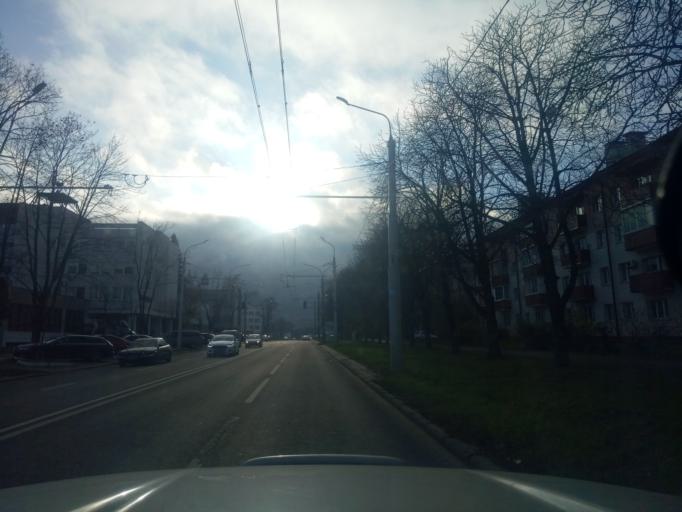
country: BY
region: Minsk
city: Syenitsa
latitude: 53.8754
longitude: 27.5039
